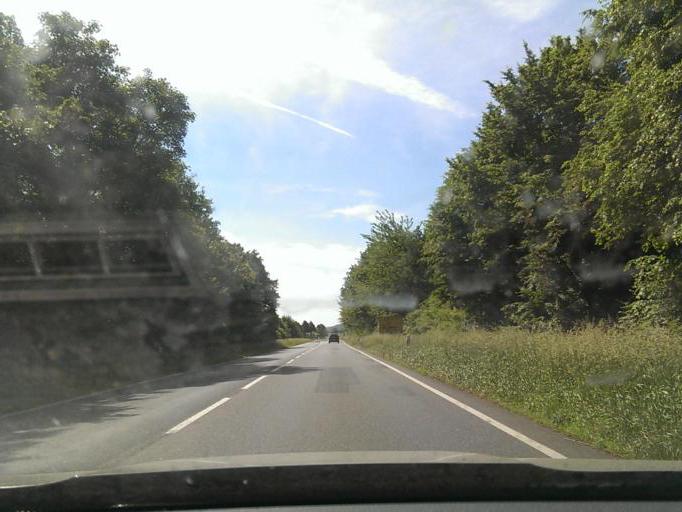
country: DE
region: Lower Saxony
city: Banteln
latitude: 52.0666
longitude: 9.7483
